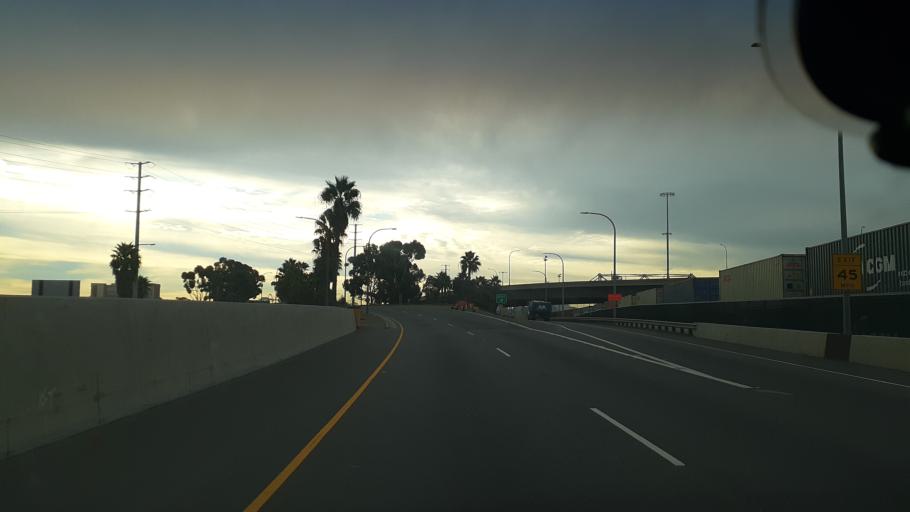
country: US
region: California
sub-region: Los Angeles County
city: Long Beach
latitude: 33.7650
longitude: -118.2073
